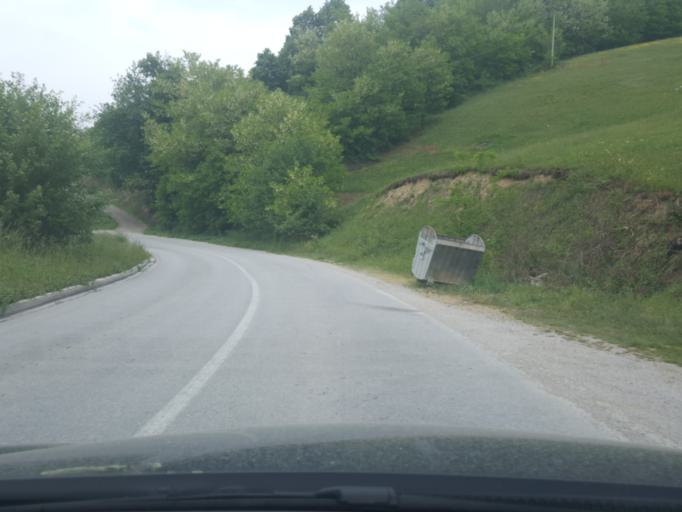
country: RS
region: Central Serbia
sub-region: Zlatiborski Okrug
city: Bajina Basta
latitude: 43.9347
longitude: 19.5712
